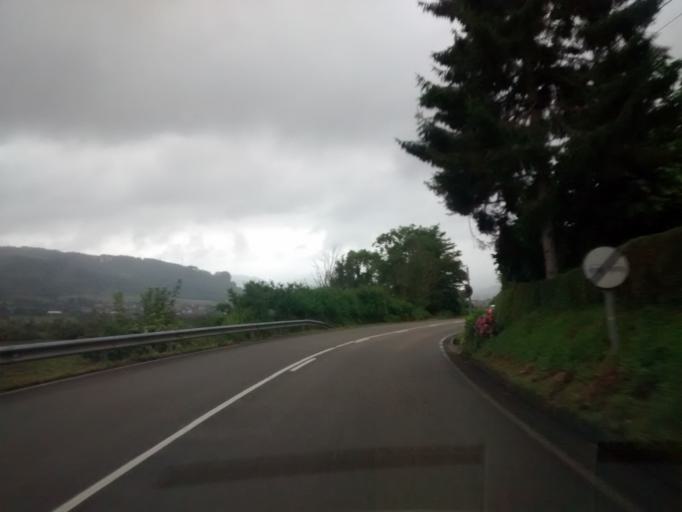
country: ES
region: Asturias
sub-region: Province of Asturias
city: Villaviciosa
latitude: 43.4977
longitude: -5.4269
